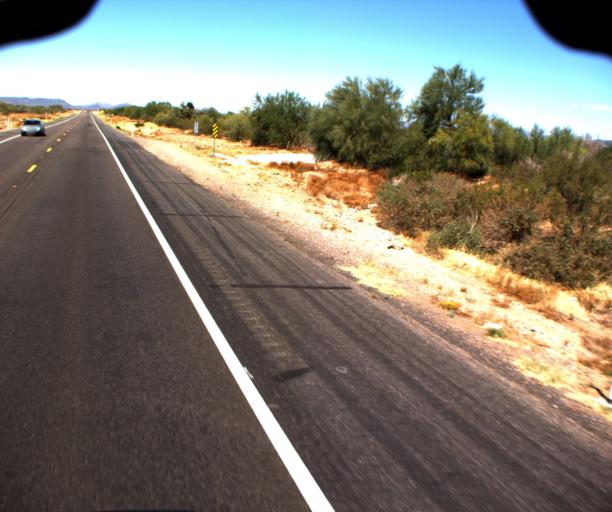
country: US
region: Arizona
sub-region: Maricopa County
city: Anthem
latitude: 33.7982
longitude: -112.1743
